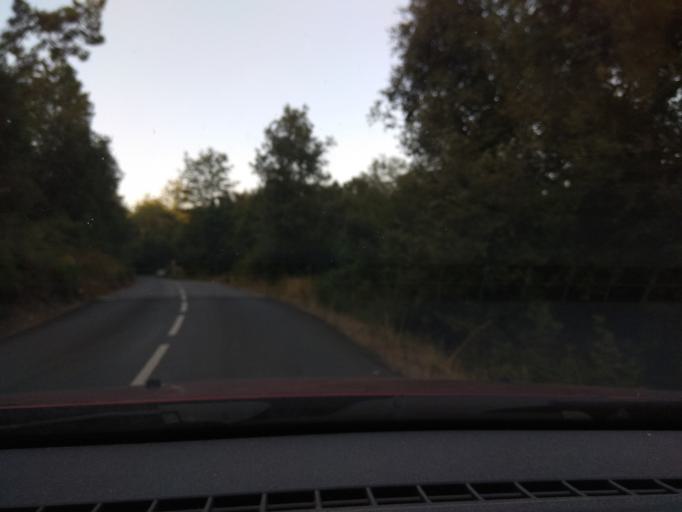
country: FR
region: Provence-Alpes-Cote d'Azur
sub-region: Departement des Alpes-Maritimes
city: Tourrettes-sur-Loup
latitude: 43.6812
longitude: 7.0519
